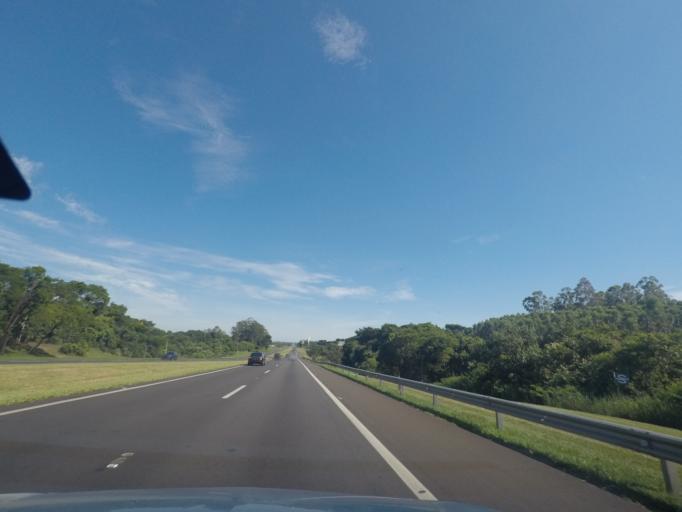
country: BR
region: Sao Paulo
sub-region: Sao Carlos
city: Sao Carlos
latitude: -22.1113
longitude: -47.8193
